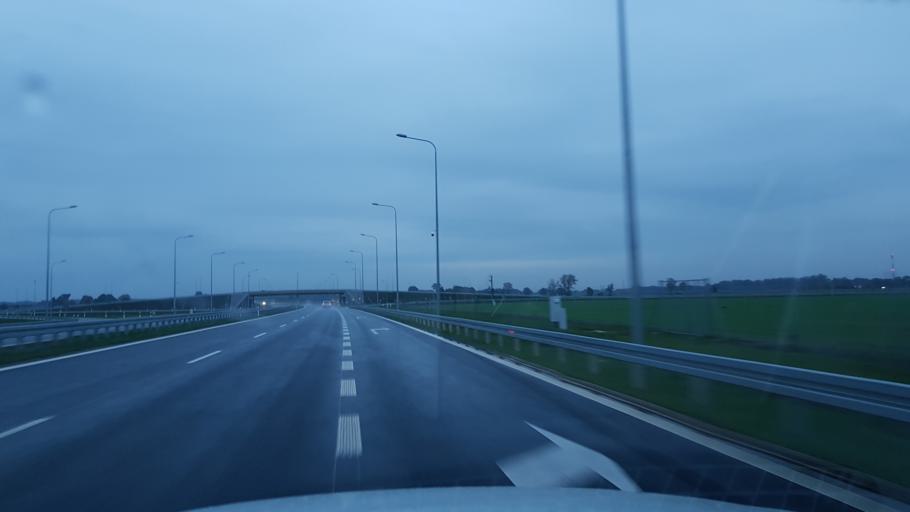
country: PL
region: West Pomeranian Voivodeship
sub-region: Powiat gryficki
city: Brojce
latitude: 53.8755
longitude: 15.3723
